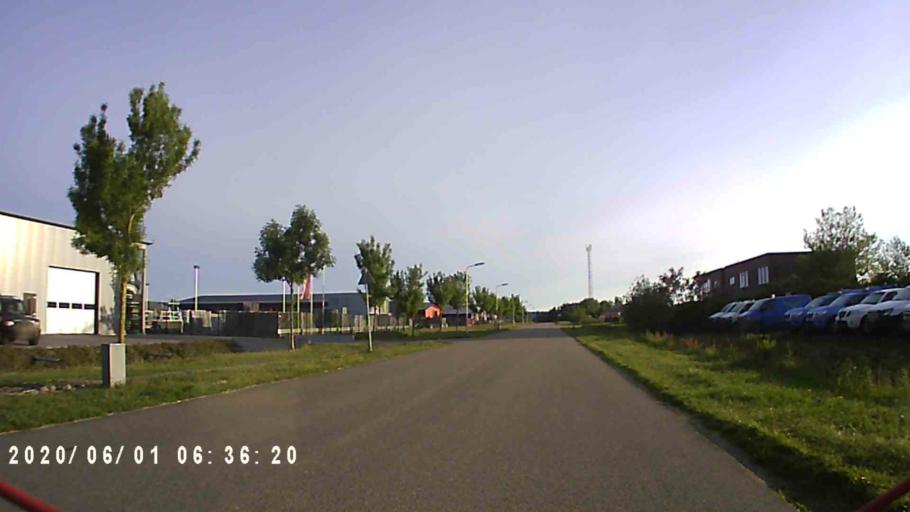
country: NL
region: Friesland
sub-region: Gemeente Kollumerland en Nieuwkruisland
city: Kollum
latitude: 53.2812
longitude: 6.1610
